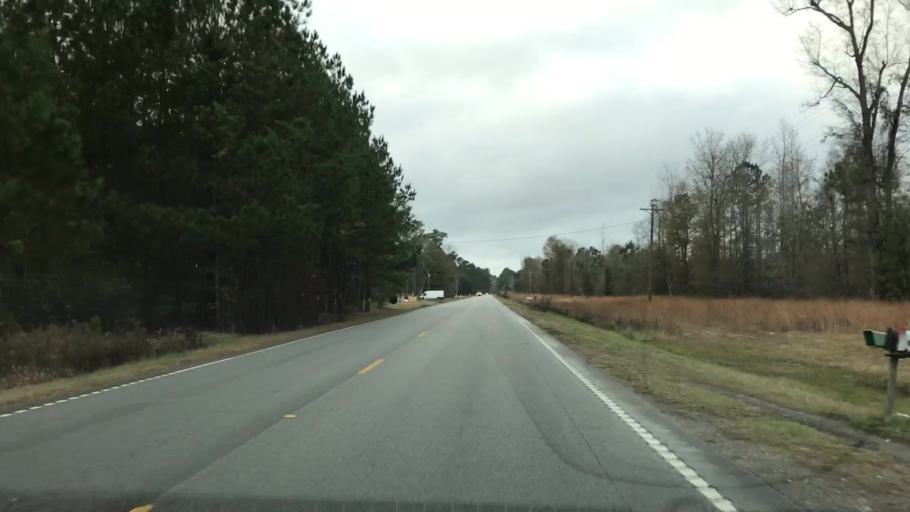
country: US
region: South Carolina
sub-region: Berkeley County
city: Saint Stephen
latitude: 33.2842
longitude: -79.7455
